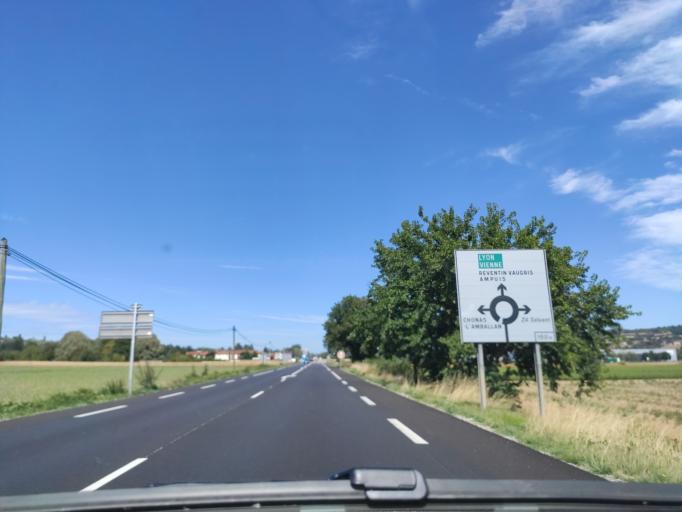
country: FR
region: Rhone-Alpes
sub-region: Departement de l'Isere
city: Reventin-Vaugris
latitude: 45.4557
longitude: 4.8245
